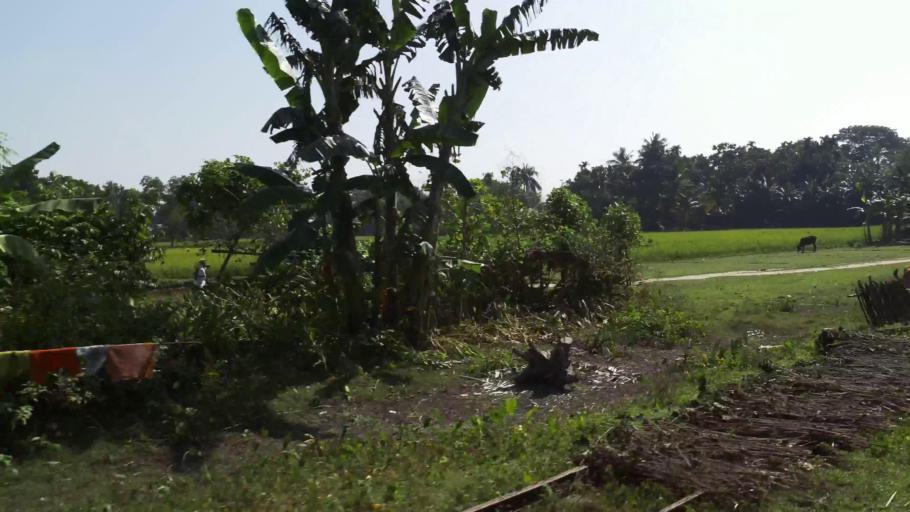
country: BD
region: Dhaka
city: Gafargaon
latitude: 24.5862
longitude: 90.5070
